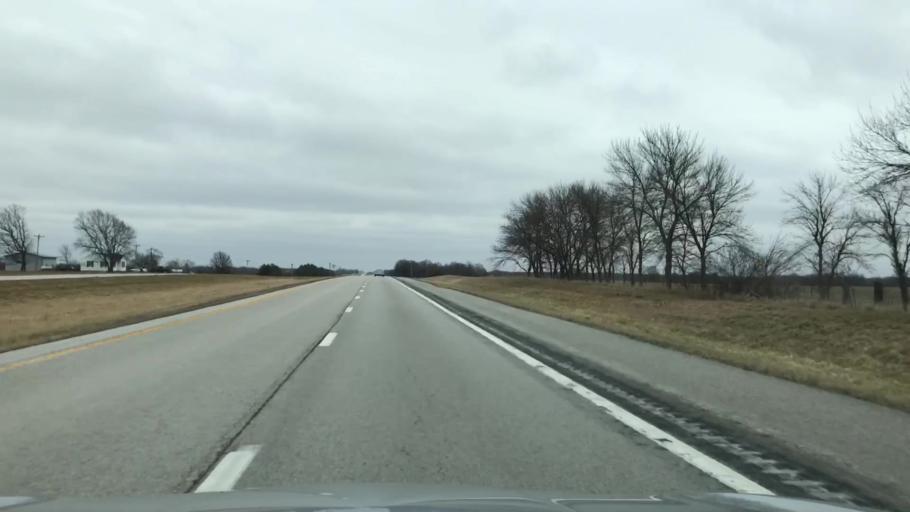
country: US
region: Missouri
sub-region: Livingston County
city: Chillicothe
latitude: 39.7771
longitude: -93.3789
